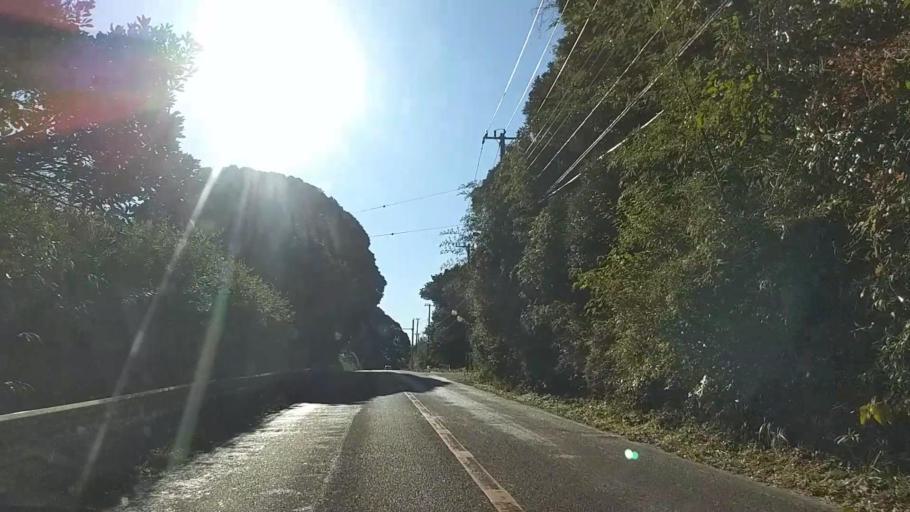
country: JP
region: Chiba
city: Kimitsu
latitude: 35.2656
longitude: 139.8735
